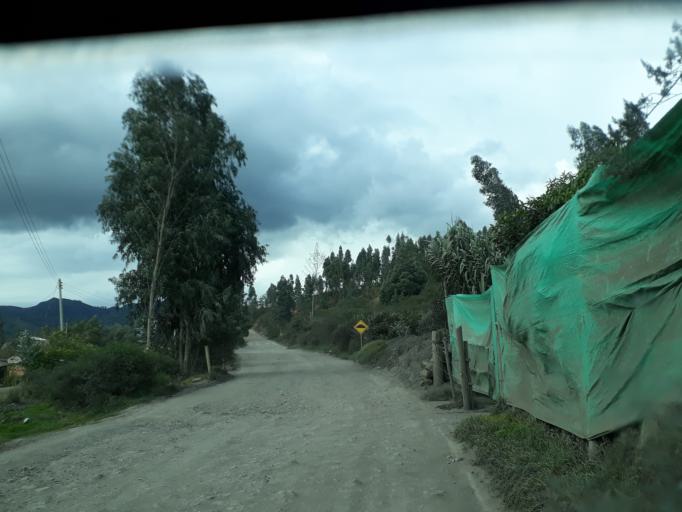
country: CO
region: Cundinamarca
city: Cucunuba
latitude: 5.2449
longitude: -73.7927
